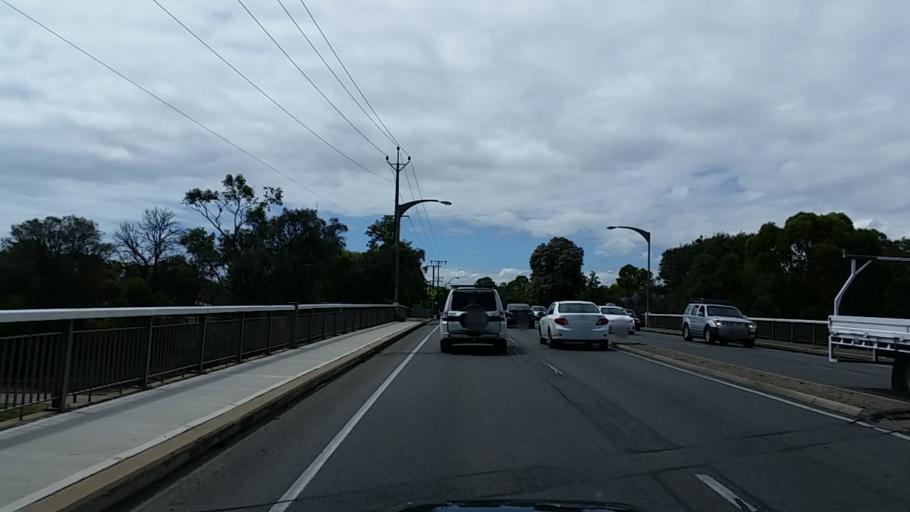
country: AU
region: South Australia
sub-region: Charles Sturt
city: Henley Beach
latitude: -34.9317
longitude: 138.5175
